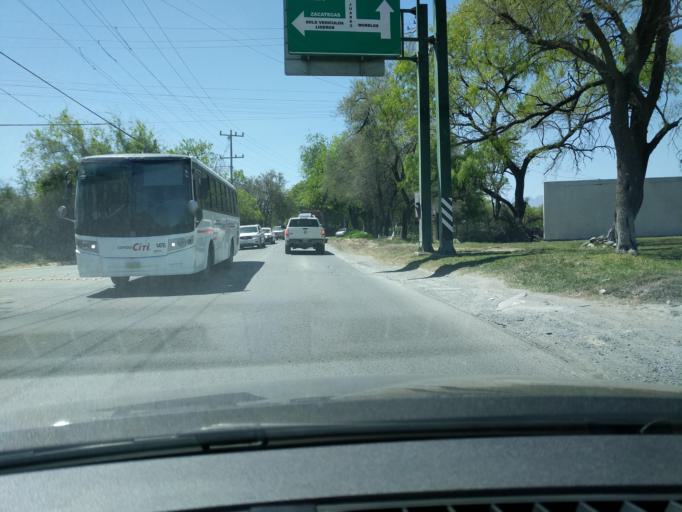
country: MX
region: Nuevo Leon
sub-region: Apodaca
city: Artemio Trevino
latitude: 25.8148
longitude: -100.1548
